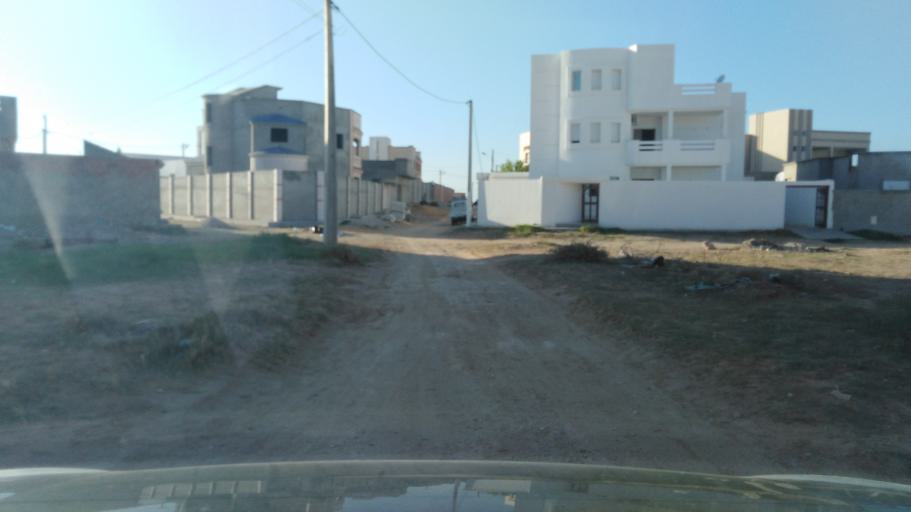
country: TN
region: Qabis
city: Gabes
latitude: 33.9502
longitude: 10.0137
